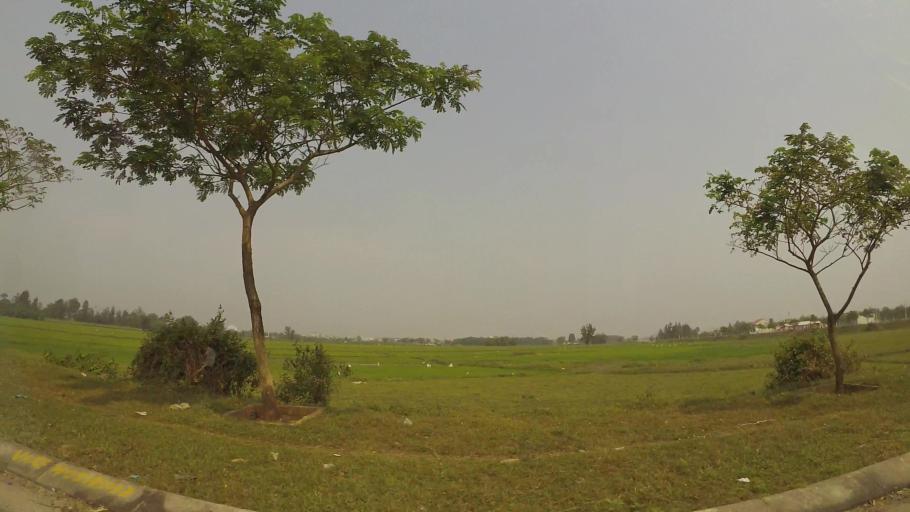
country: VN
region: Da Nang
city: Cam Le
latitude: 15.9714
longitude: 108.2223
